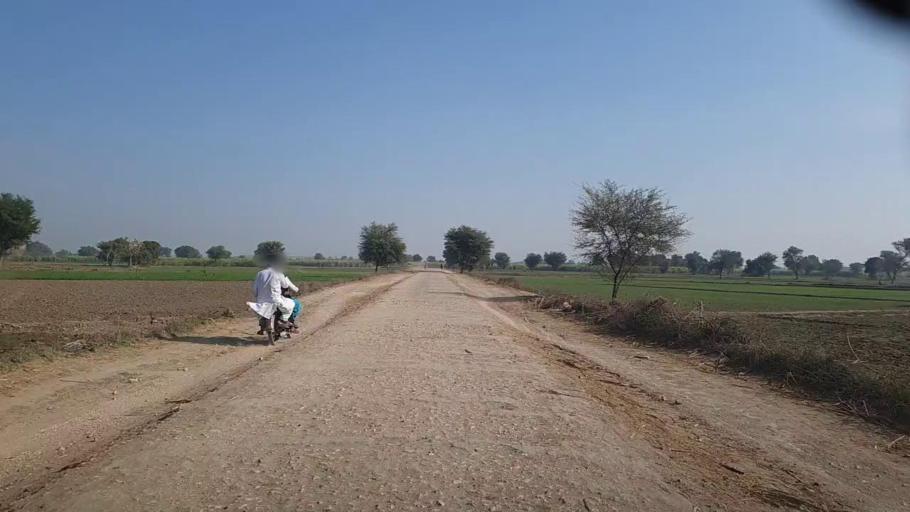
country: PK
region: Sindh
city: Darya Khan Marri
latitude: 26.6711
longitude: 68.3269
